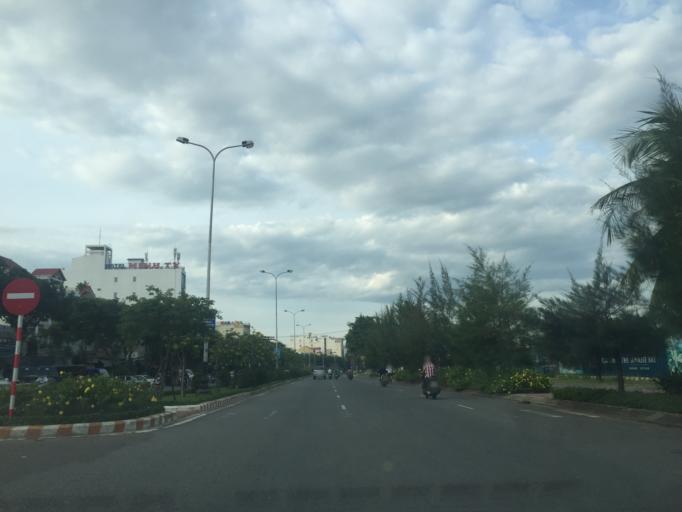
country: VN
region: Da Nang
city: Da Nang
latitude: 16.0849
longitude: 108.2138
